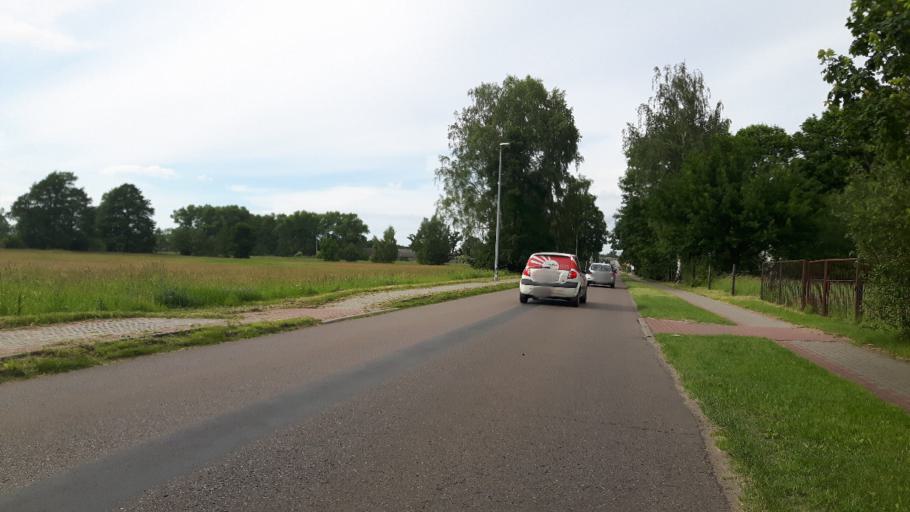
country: PL
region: West Pomeranian Voivodeship
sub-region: Powiat goleniowski
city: Goleniow
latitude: 53.4496
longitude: 14.7429
